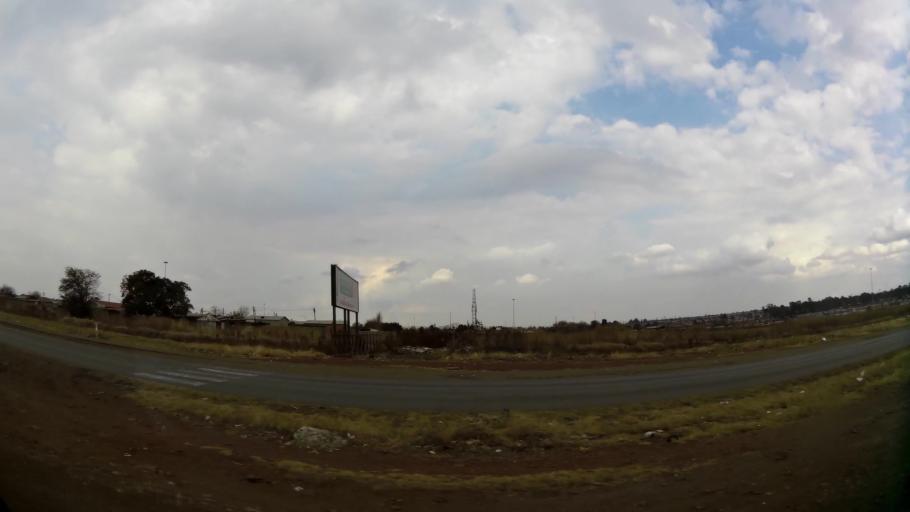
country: ZA
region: Gauteng
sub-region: Sedibeng District Municipality
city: Vanderbijlpark
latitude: -26.6618
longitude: 27.8439
